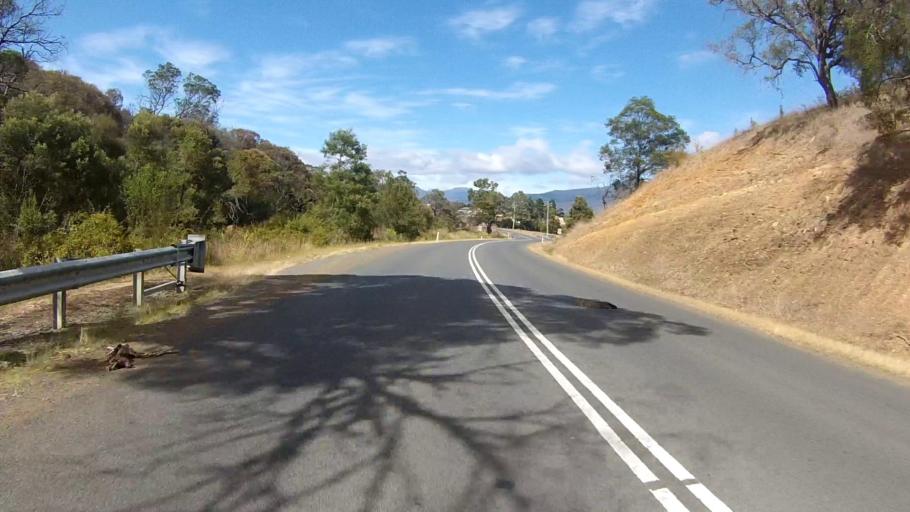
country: AU
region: Tasmania
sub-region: Brighton
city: Old Beach
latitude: -42.7443
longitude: 147.2832
